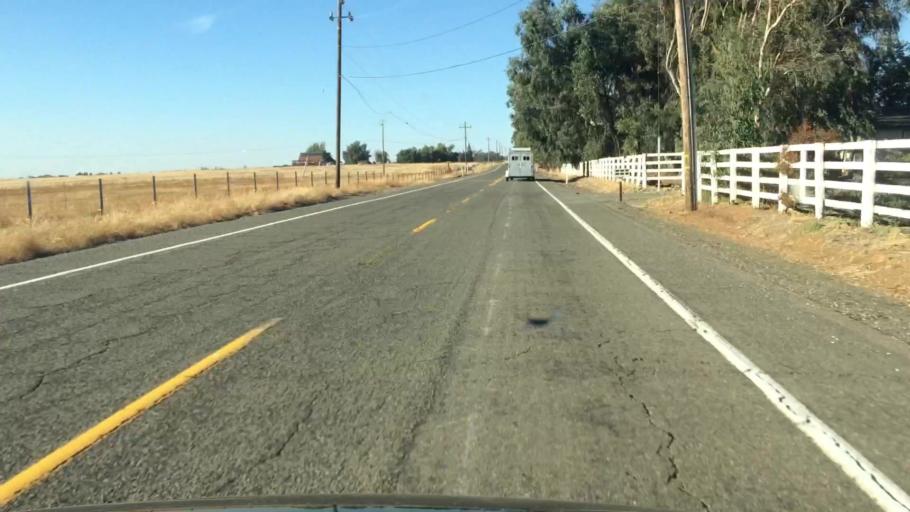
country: US
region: California
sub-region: Sacramento County
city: Clay
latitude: 38.4019
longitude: -121.1715
